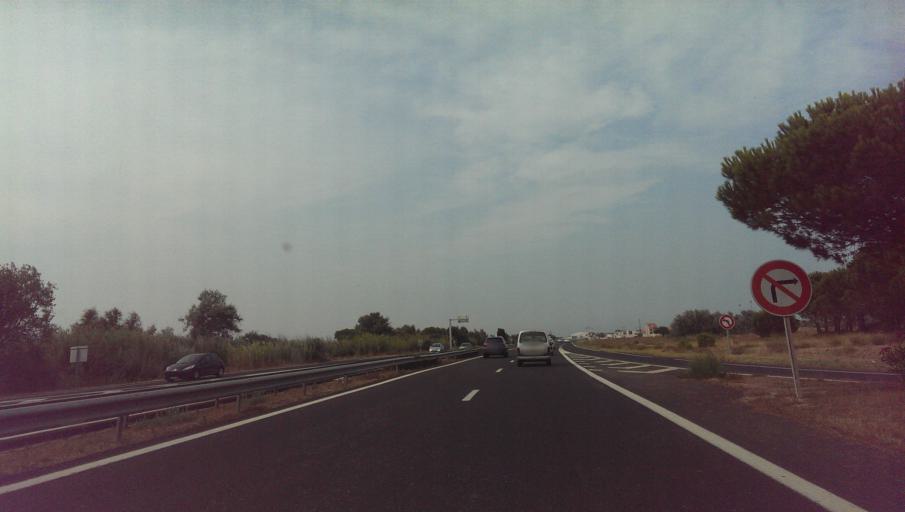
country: FR
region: Languedoc-Roussillon
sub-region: Departement des Pyrenees-Orientales
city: Le Barcares
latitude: 42.7941
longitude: 3.0257
